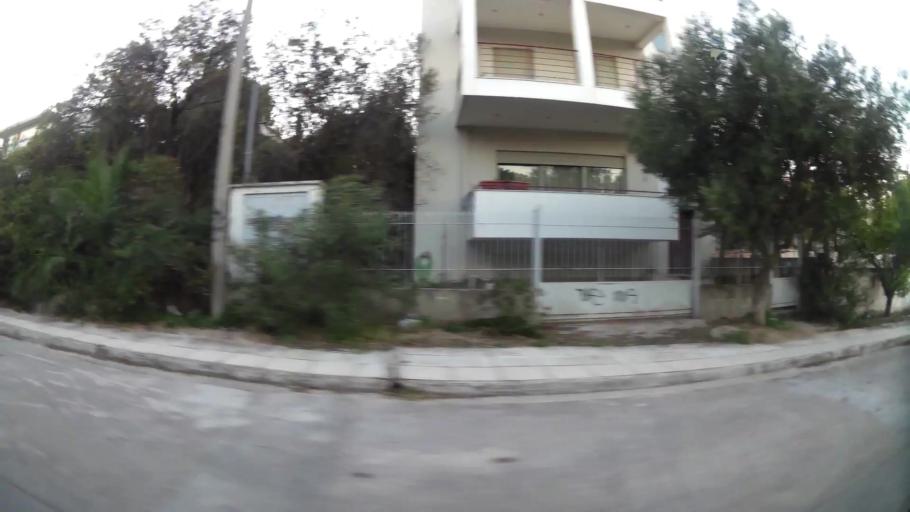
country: GR
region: Attica
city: Pefki
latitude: 38.0626
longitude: 23.7887
